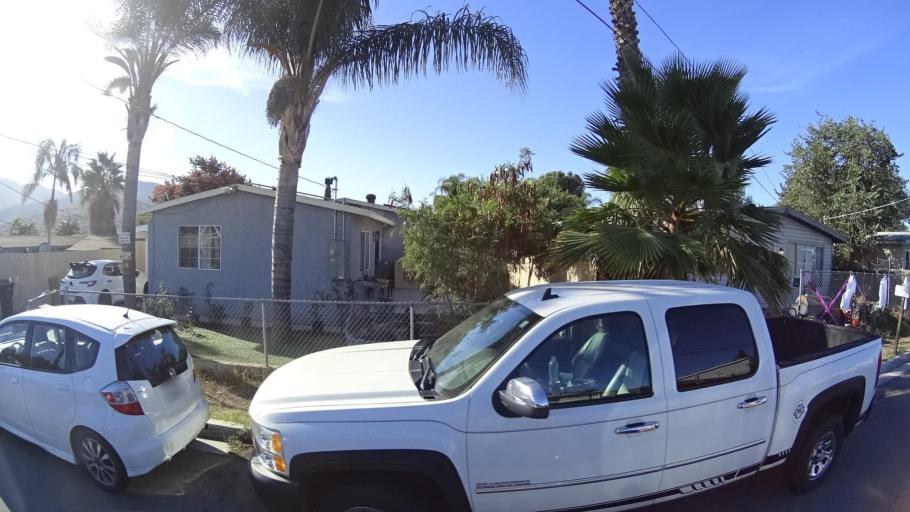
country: US
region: California
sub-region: San Diego County
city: La Presa
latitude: 32.7094
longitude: -116.9853
